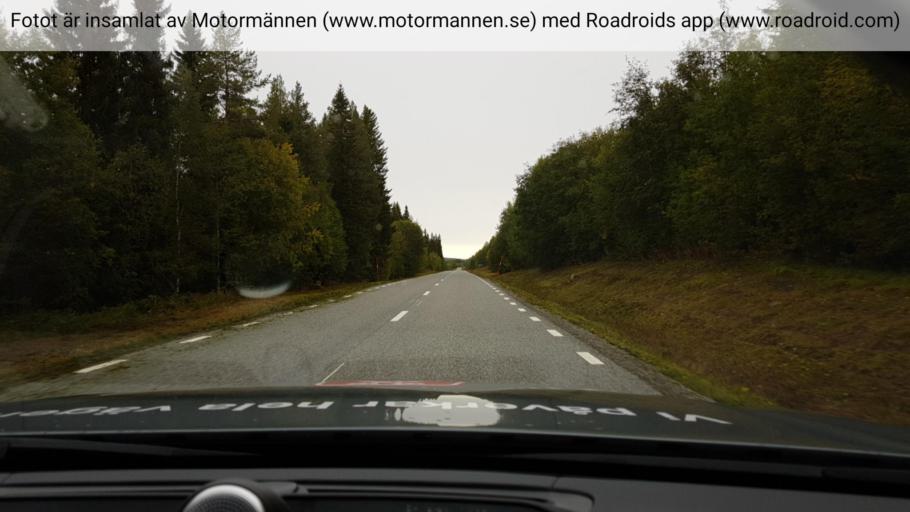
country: SE
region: Jaemtland
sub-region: Stroemsunds Kommun
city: Stroemsund
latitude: 63.9960
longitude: 15.5117
